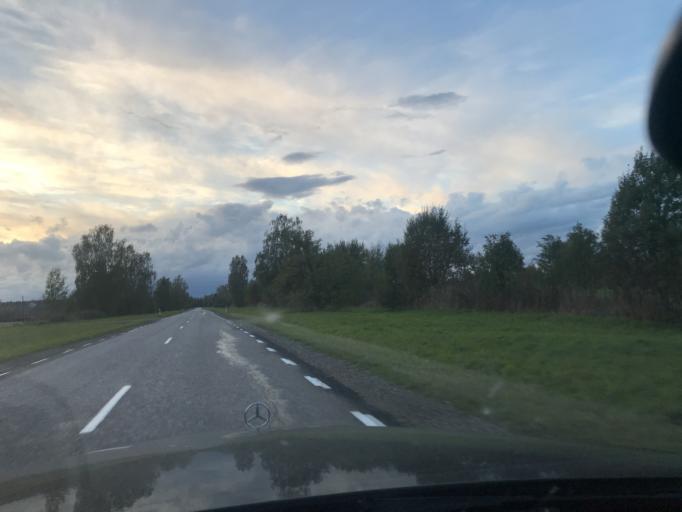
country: EE
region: Valgamaa
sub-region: Torva linn
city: Torva
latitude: 58.0103
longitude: 26.1881
